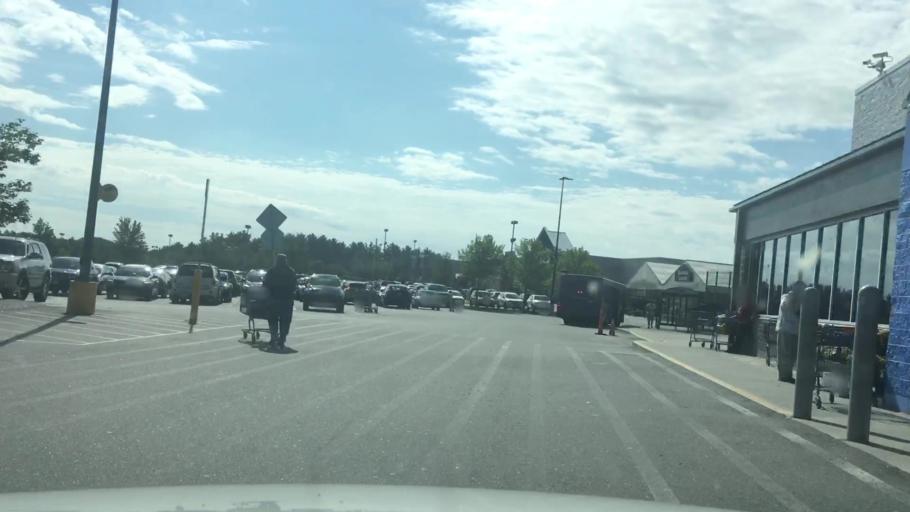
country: US
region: Maine
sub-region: Androscoggin County
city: Auburn
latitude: 44.1178
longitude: -70.2373
